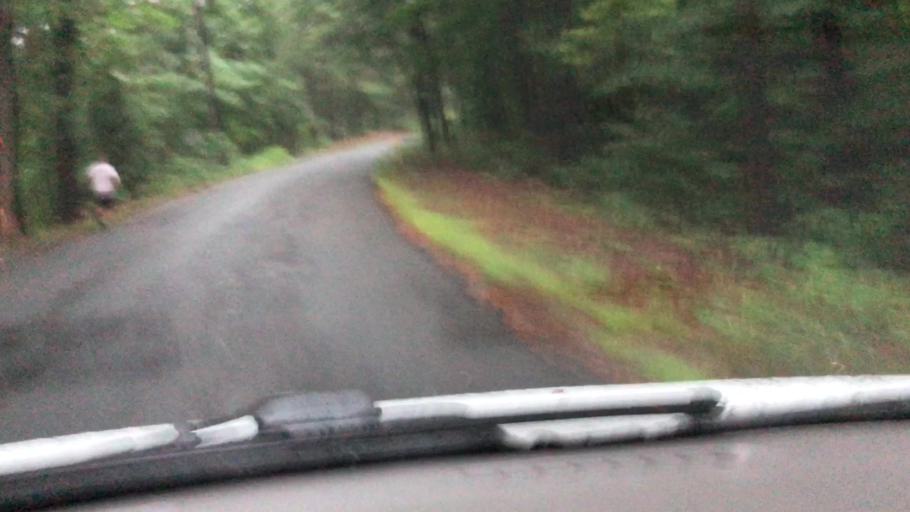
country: US
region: Massachusetts
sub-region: Hampshire County
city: Southampton
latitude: 42.2500
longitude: -72.7157
